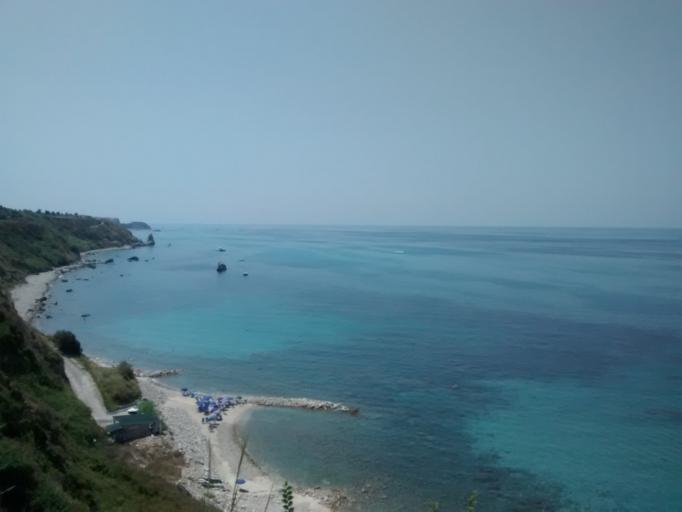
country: IT
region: Calabria
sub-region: Provincia di Vibo-Valentia
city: Parghelia
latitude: 38.6906
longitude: 15.9376
